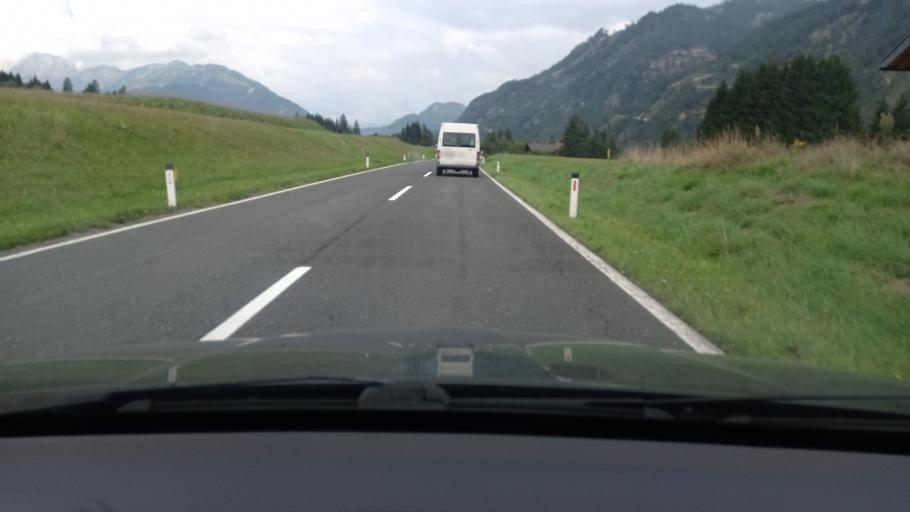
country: AT
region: Carinthia
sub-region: Politischer Bezirk Hermagor
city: Hermagor
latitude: 46.6634
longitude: 13.3080
